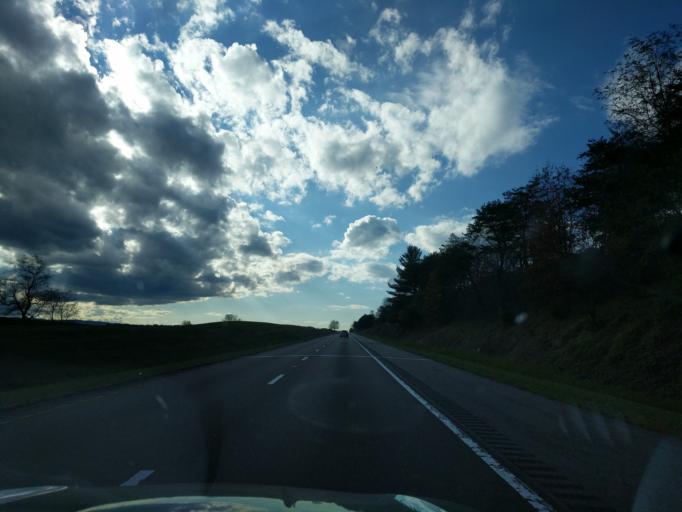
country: US
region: Virginia
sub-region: Wythe County
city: Rural Retreat
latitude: 36.9216
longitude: -81.2293
